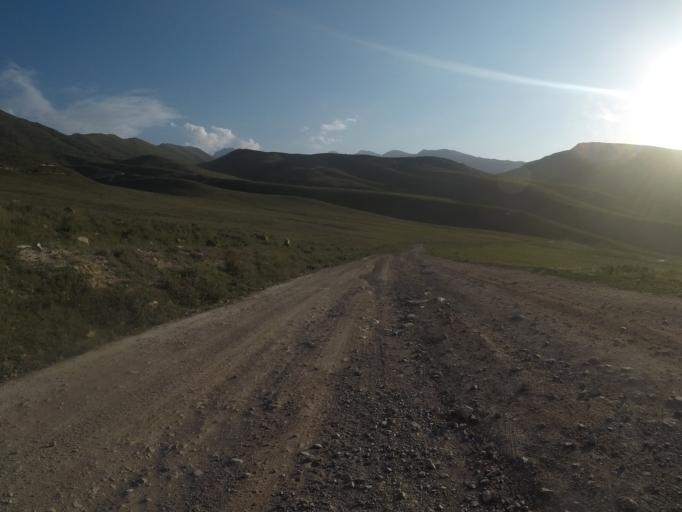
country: KG
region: Chuy
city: Bishkek
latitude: 42.6545
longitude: 74.6604
